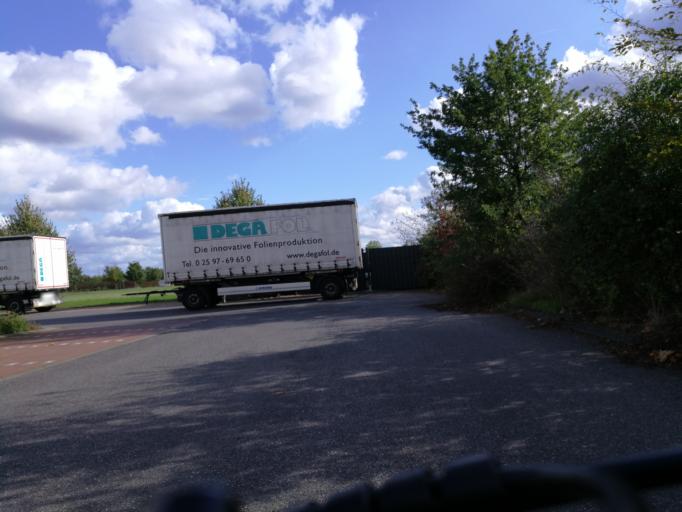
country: DE
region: North Rhine-Westphalia
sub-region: Regierungsbezirk Dusseldorf
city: Dusseldorf
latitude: 51.1448
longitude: 6.7539
